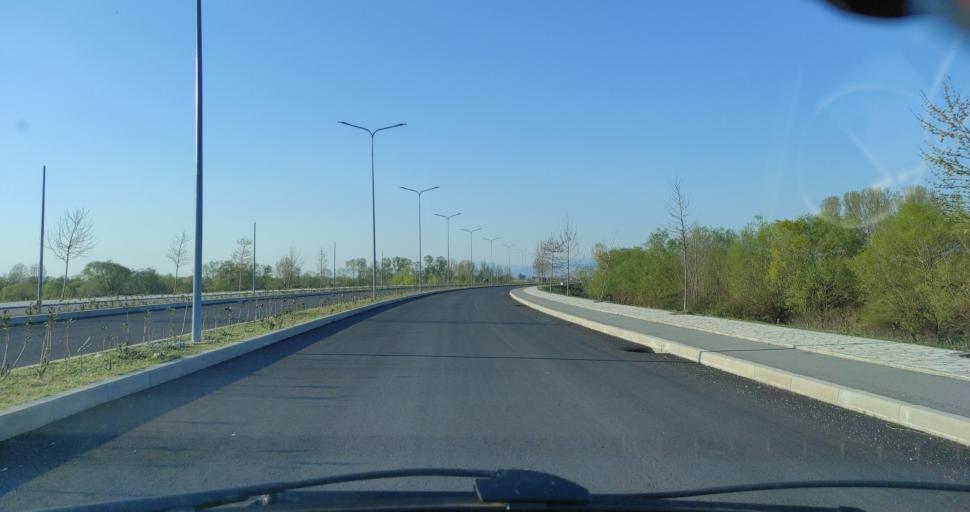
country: AL
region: Shkoder
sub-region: Rrethi i Shkodres
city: Shkoder
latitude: 42.0669
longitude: 19.4896
